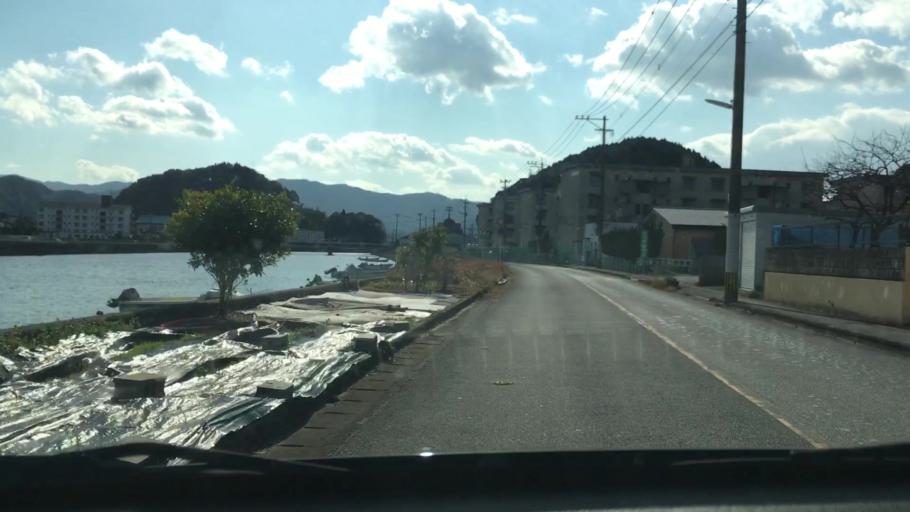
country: JP
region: Oita
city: Saiki
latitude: 32.9651
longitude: 131.9132
